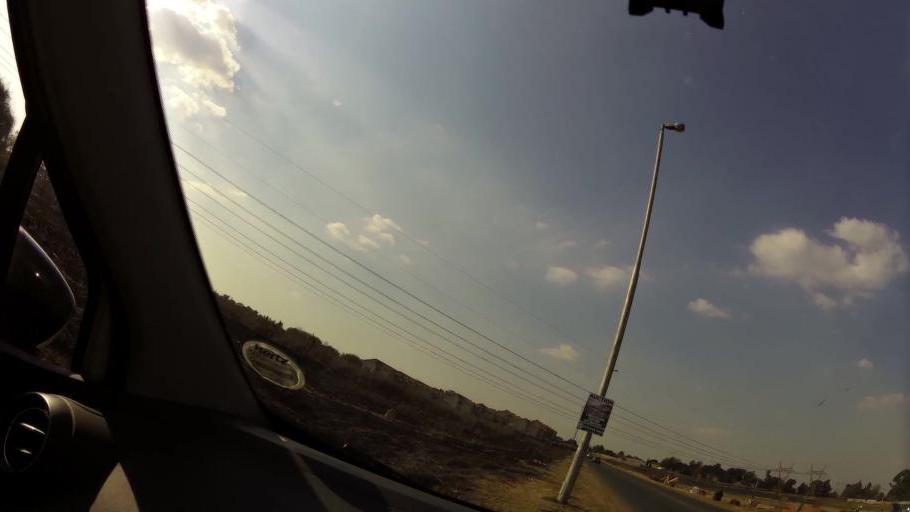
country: ZA
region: Gauteng
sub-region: Ekurhuleni Metropolitan Municipality
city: Benoni
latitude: -26.1409
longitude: 28.2859
